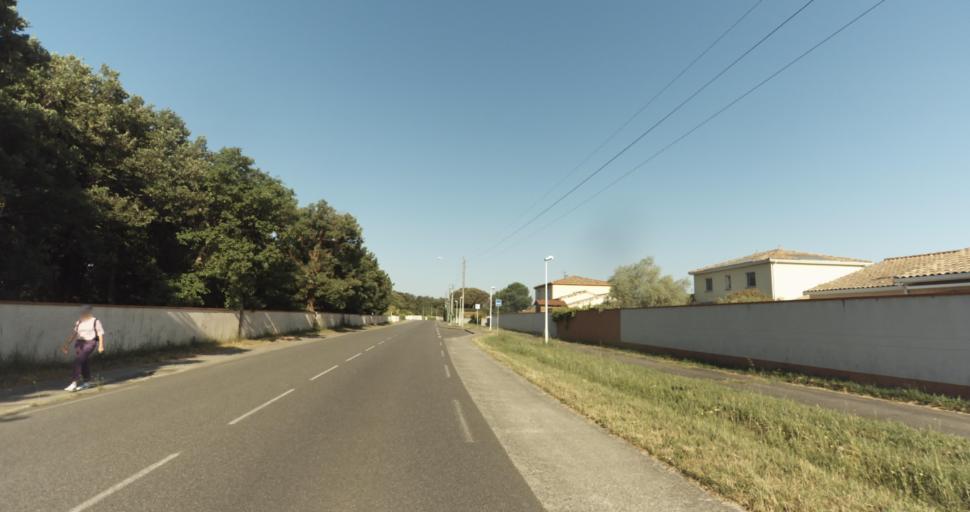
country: FR
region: Midi-Pyrenees
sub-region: Departement de la Haute-Garonne
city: La Salvetat-Saint-Gilles
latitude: 43.5692
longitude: 1.2421
